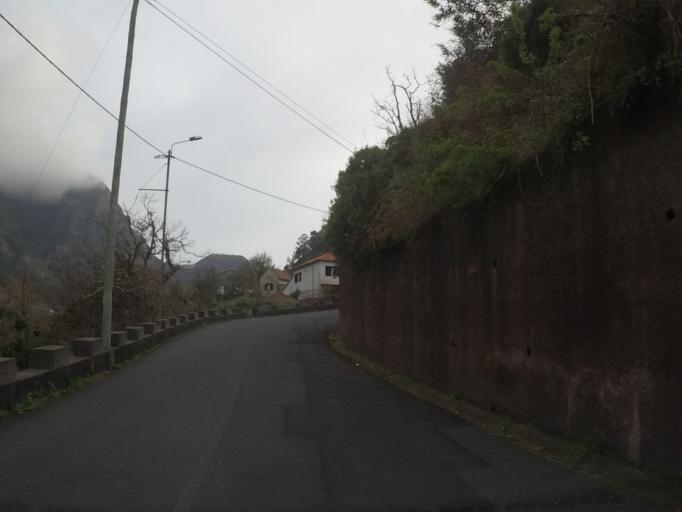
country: PT
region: Madeira
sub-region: Camara de Lobos
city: Curral das Freiras
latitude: 32.7339
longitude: -16.9703
